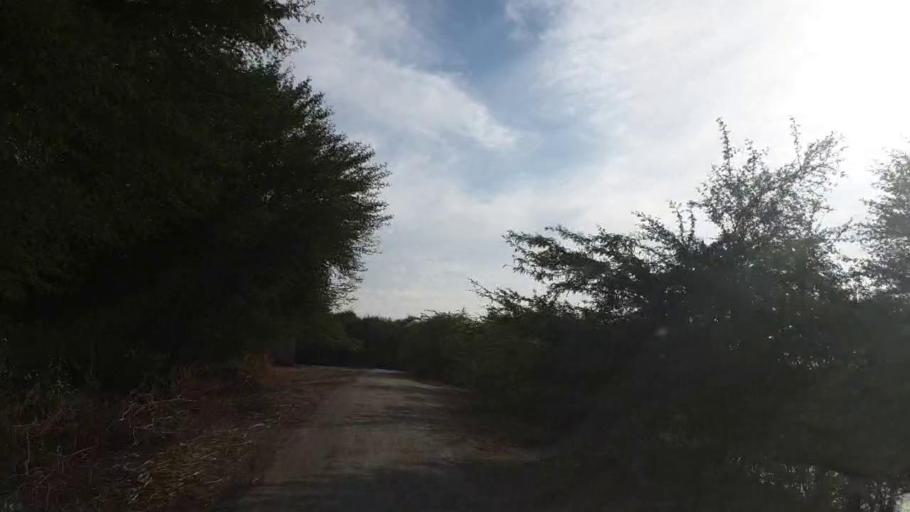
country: PK
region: Sindh
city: Pithoro
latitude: 25.6394
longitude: 69.3611
